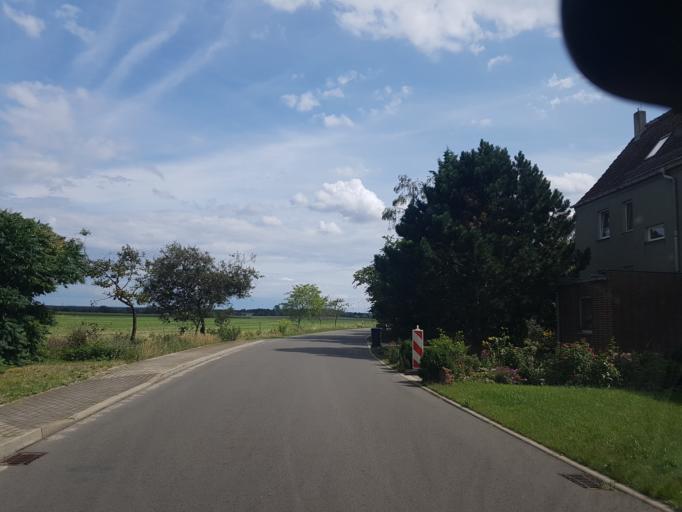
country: DE
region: Brandenburg
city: Schlieben
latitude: 51.6916
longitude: 13.3325
